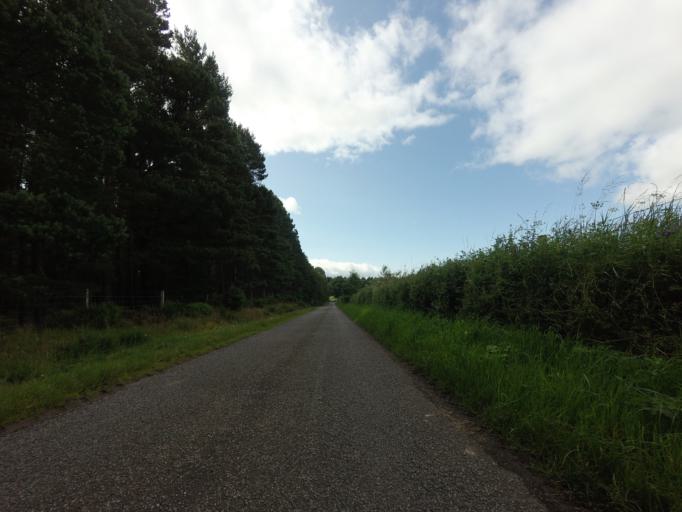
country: GB
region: Scotland
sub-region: Highland
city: Nairn
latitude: 57.5629
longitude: -3.8671
